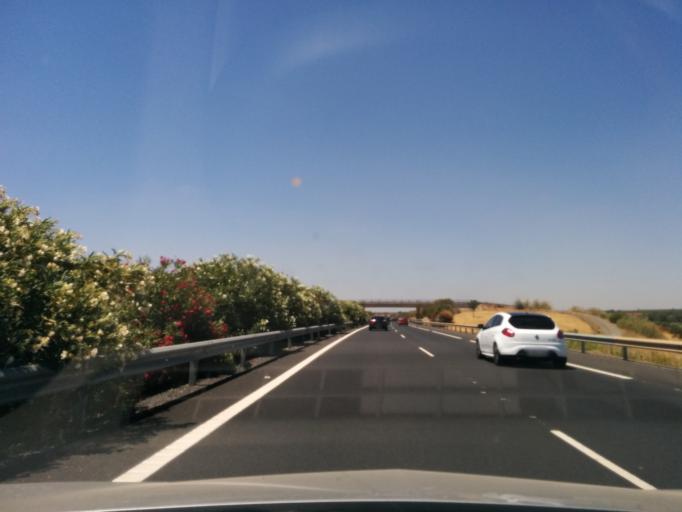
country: ES
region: Andalusia
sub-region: Provincia de Huelva
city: Bonares
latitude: 37.3413
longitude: -6.6920
